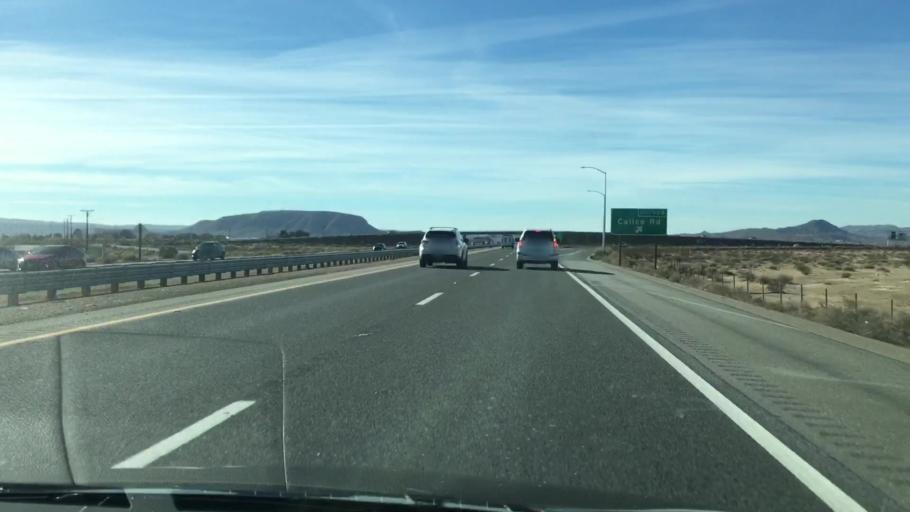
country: US
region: California
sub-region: San Bernardino County
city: Barstow
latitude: 34.9101
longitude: -116.8331
